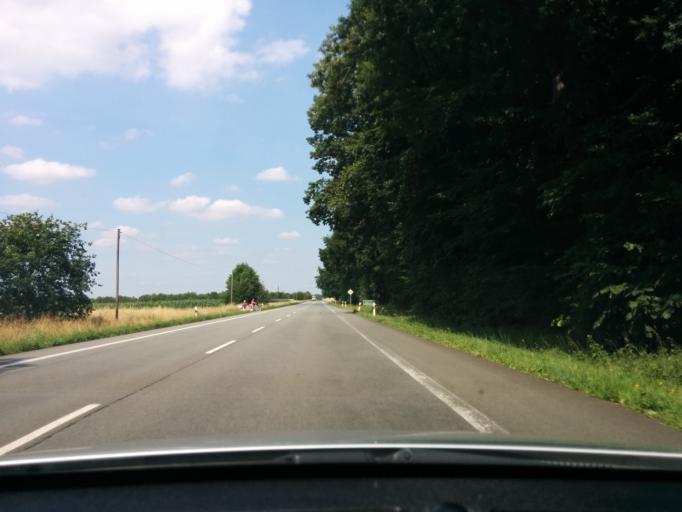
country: DE
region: North Rhine-Westphalia
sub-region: Regierungsbezirk Munster
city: Wettringen
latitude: 52.1879
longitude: 7.2847
